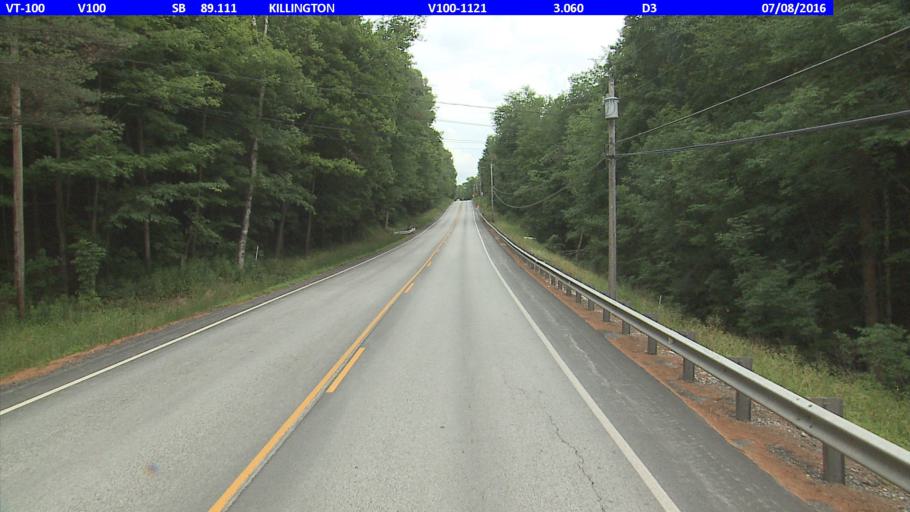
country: US
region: Vermont
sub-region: Rutland County
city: Rutland
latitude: 43.7058
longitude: -72.8238
